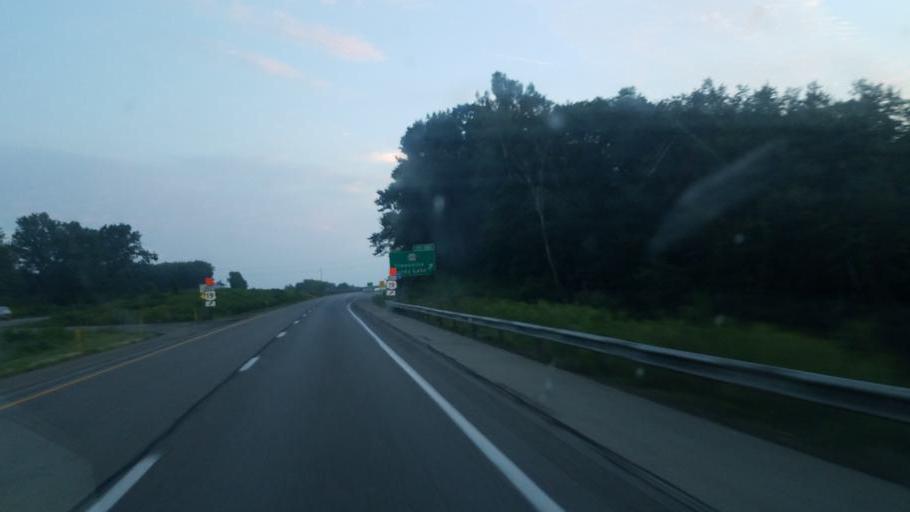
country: US
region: Pennsylvania
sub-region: Mercer County
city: Stoneboro
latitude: 41.3795
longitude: -80.1584
